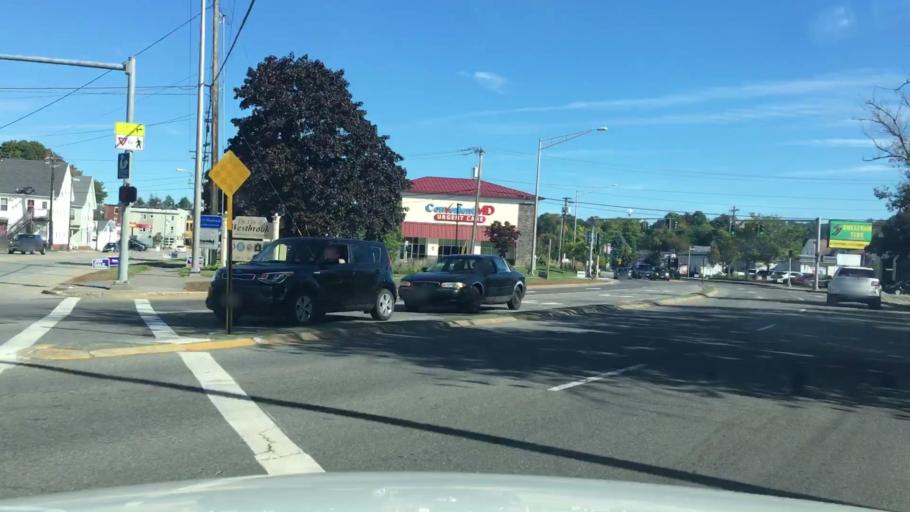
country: US
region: Maine
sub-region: Cumberland County
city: Westbrook
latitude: 43.6770
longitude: -70.3724
